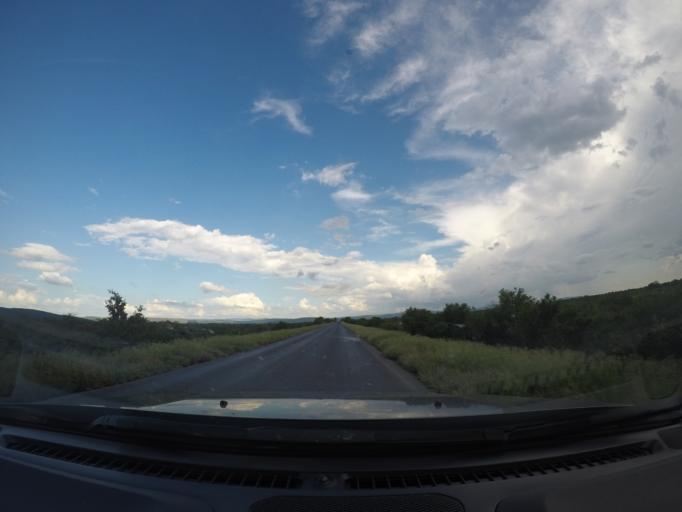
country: BR
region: Bahia
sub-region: Ibotirama
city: Ibotirama
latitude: -12.1602
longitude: -43.2923
